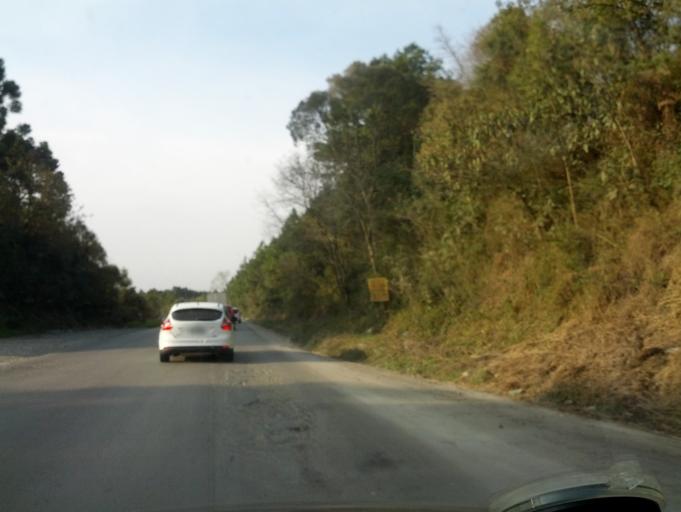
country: BR
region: Santa Catarina
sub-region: Otacilio Costa
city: Otacilio Costa
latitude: -27.5542
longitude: -50.1485
